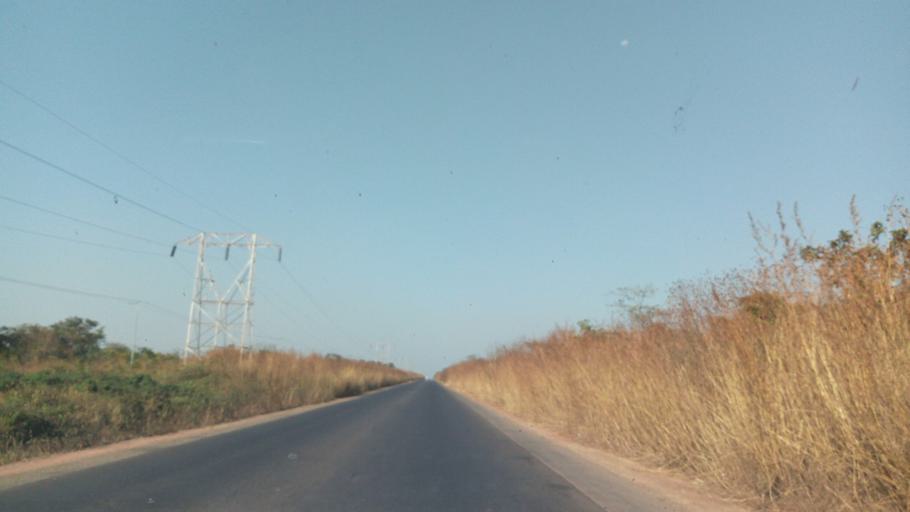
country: CD
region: Katanga
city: Likasi
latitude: -11.0018
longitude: 26.8643
